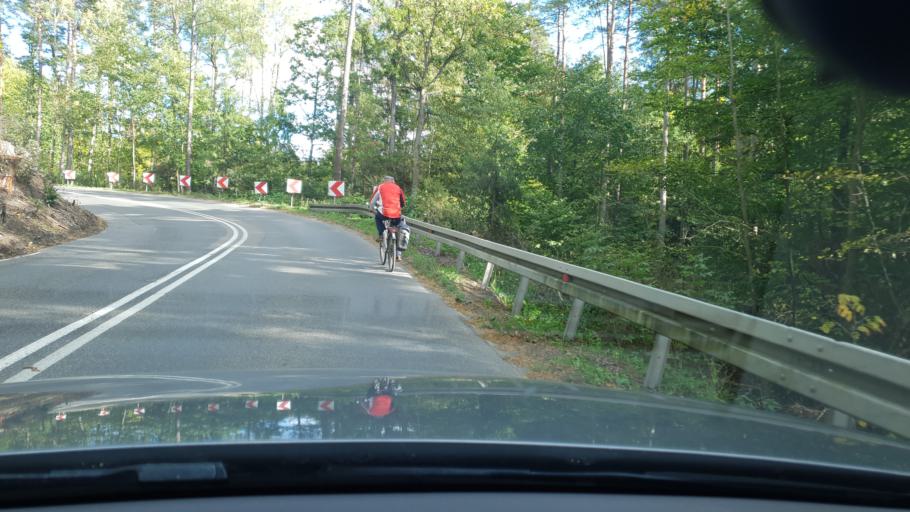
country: PL
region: Pomeranian Voivodeship
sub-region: Powiat wejherowski
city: Koleczkowo
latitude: 54.4987
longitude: 18.3621
